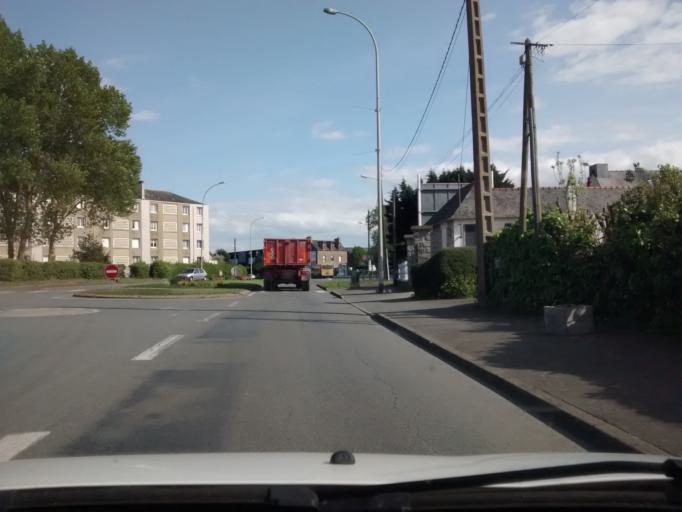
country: FR
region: Brittany
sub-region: Departement d'Ille-et-Vilaine
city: Dinard
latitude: 48.6249
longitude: -2.0684
